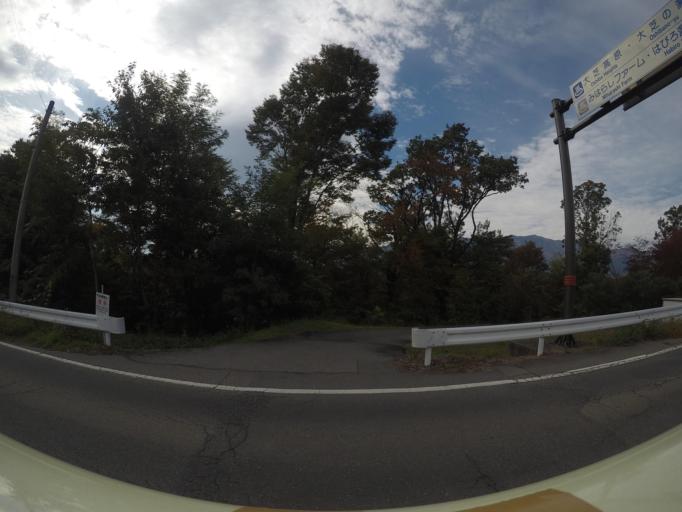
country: JP
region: Nagano
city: Ina
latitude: 35.8494
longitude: 137.9479
